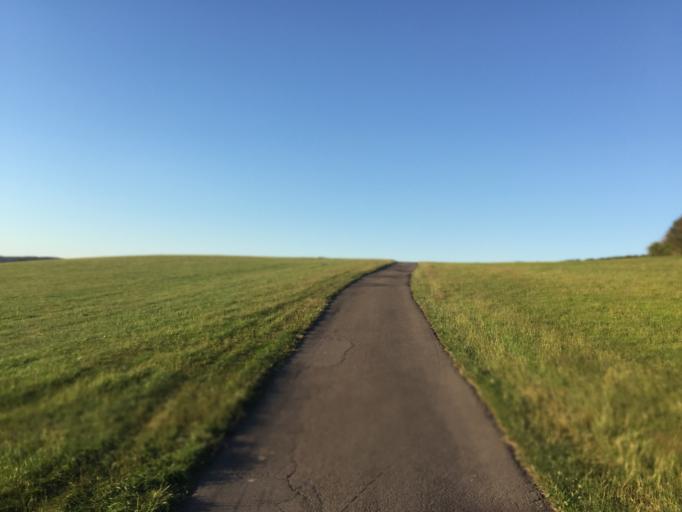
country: DE
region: North Rhine-Westphalia
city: Meinerzhagen
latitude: 51.1181
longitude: 7.6518
